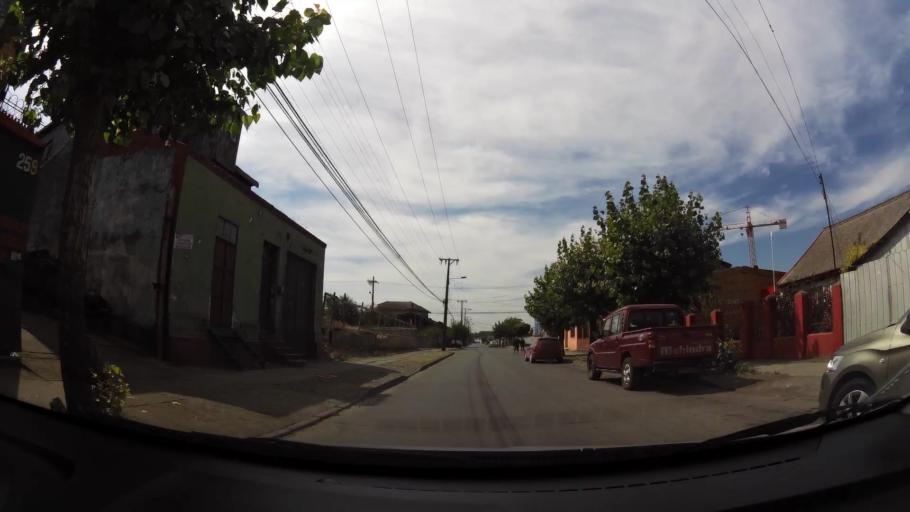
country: CL
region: Biobio
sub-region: Provincia de Concepcion
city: Talcahuano
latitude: -36.7229
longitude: -73.1240
